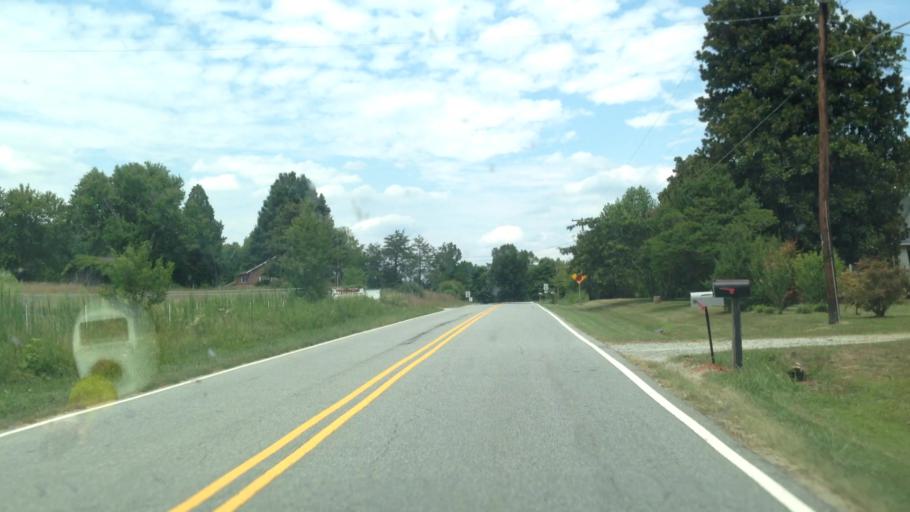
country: US
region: North Carolina
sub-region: Stokes County
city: Walnut Cove
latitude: 36.2473
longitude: -80.0973
